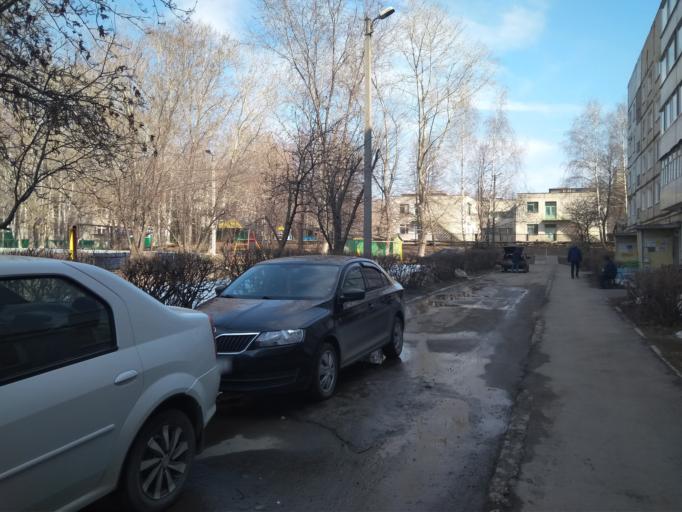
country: RU
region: Ulyanovsk
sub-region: Ulyanovskiy Rayon
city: Ulyanovsk
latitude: 54.2593
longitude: 48.3300
